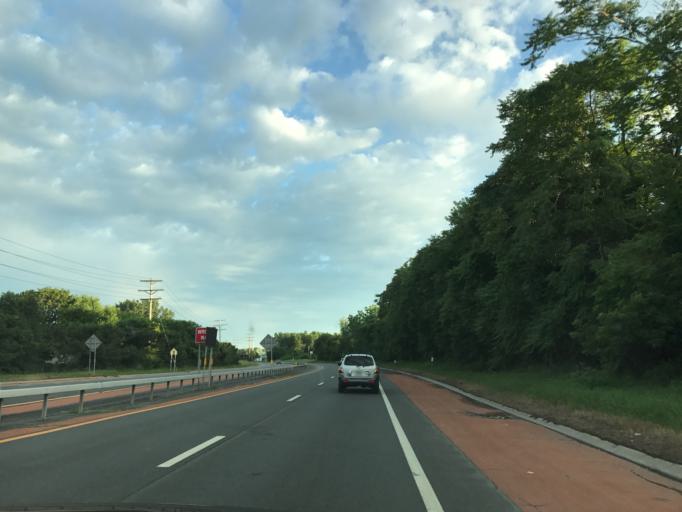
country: US
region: New York
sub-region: Albany County
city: Cohoes
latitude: 42.7680
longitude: -73.6983
